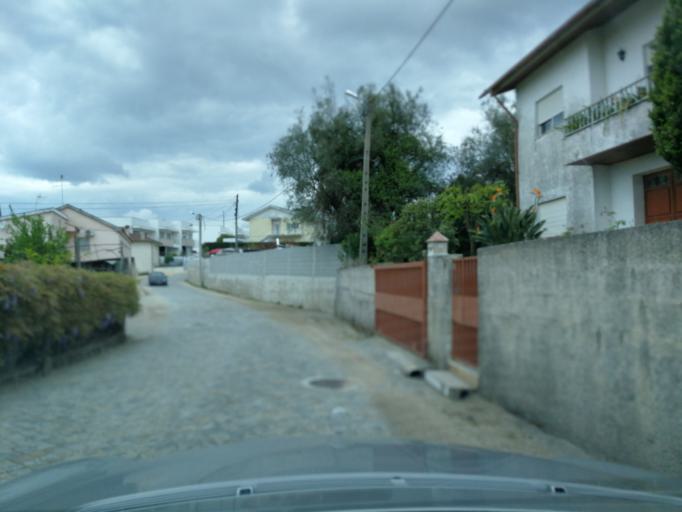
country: PT
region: Braga
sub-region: Braga
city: Braga
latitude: 41.5263
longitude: -8.3956
